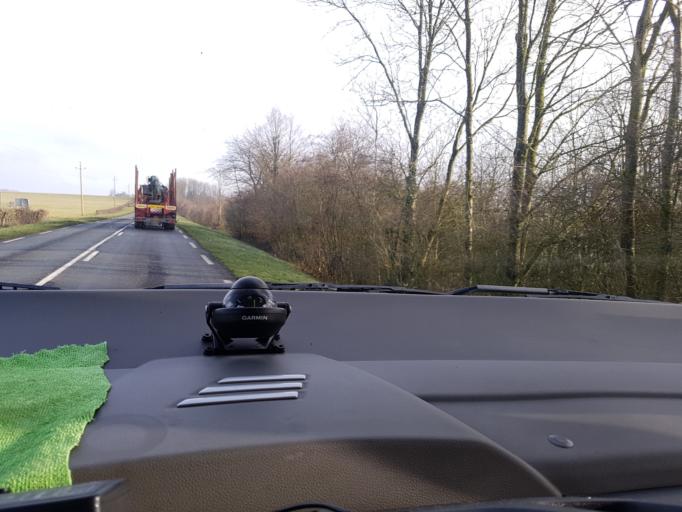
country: FR
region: Champagne-Ardenne
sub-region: Departement des Ardennes
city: Signy-le-Petit
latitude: 49.8652
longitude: 4.2256
